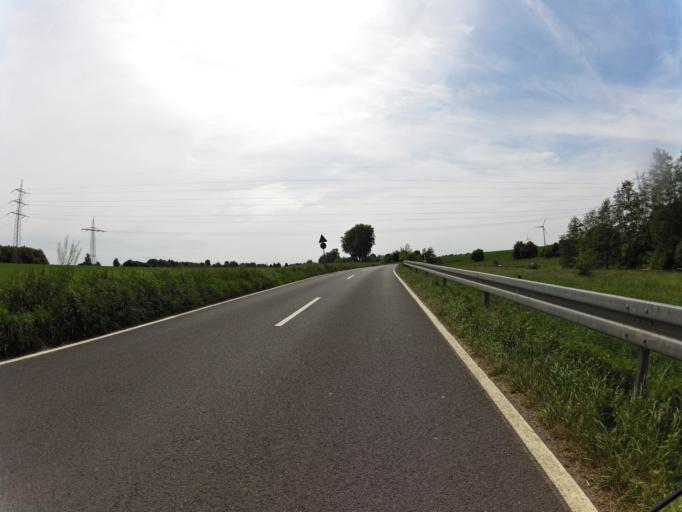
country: DE
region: North Rhine-Westphalia
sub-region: Regierungsbezirk Koln
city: Eschweiler
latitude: 50.8418
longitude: 6.2212
